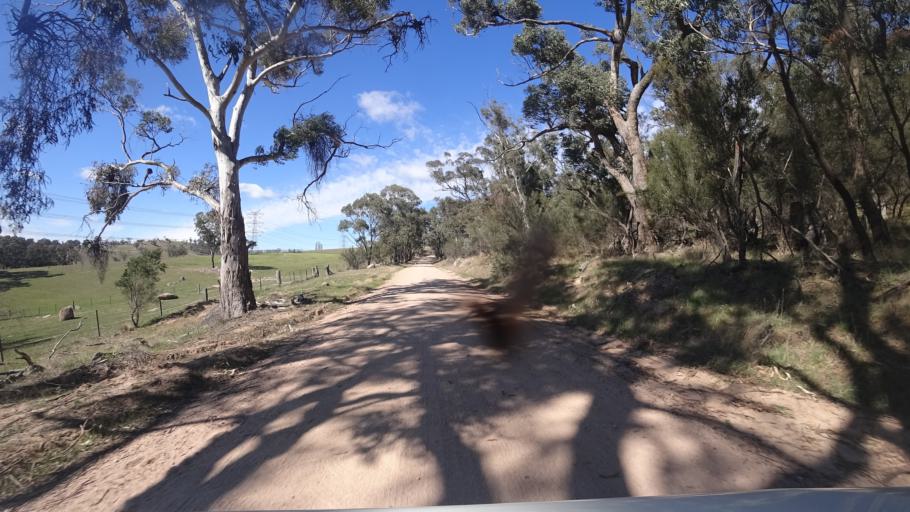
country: AU
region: New South Wales
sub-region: Lithgow
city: Bowenfels
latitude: -33.5352
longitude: 149.9334
